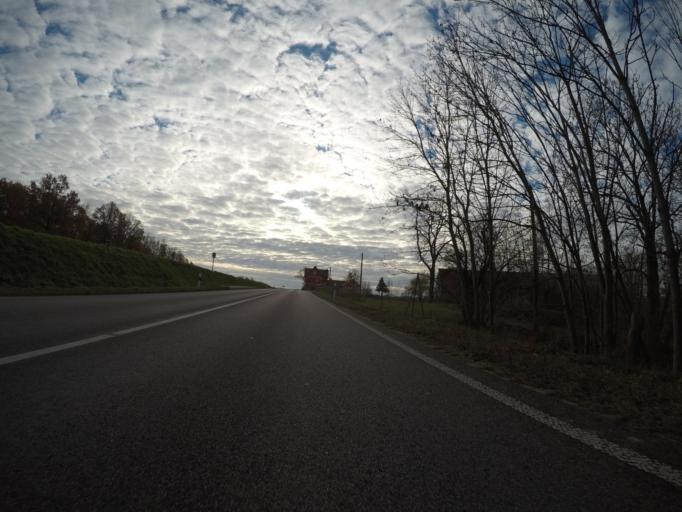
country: DE
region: Thuringia
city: Saara
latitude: 50.9444
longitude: 12.4242
